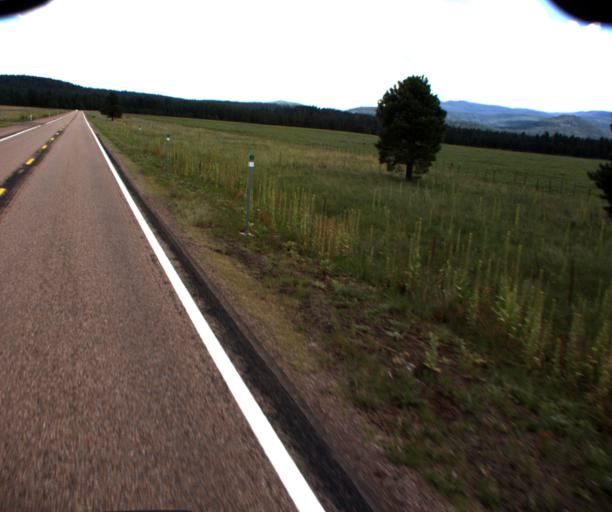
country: US
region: Arizona
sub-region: Navajo County
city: Pinetop-Lakeside
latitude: 34.0435
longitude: -109.6872
